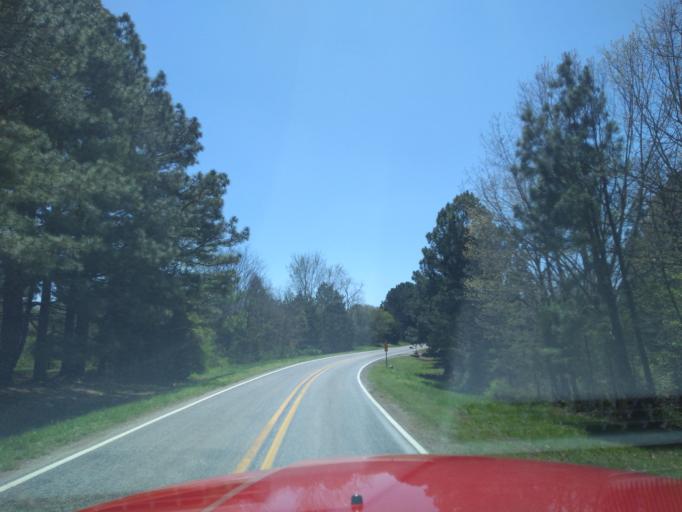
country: US
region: Arkansas
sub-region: Washington County
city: West Fork
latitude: 35.8330
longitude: -94.2671
